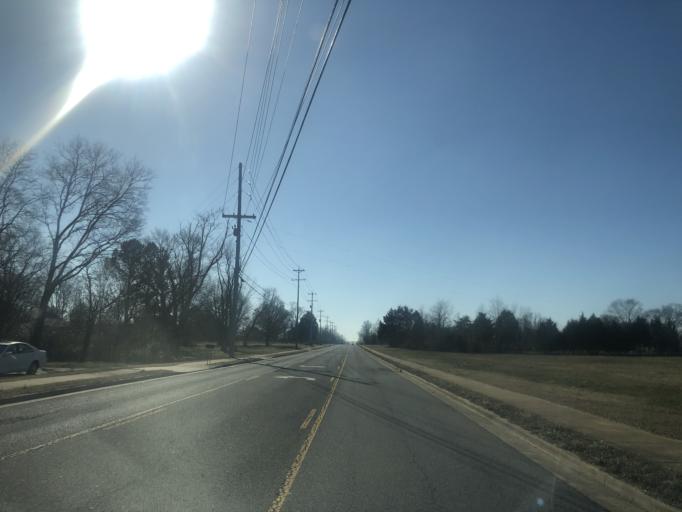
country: US
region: Tennessee
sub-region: Rutherford County
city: Smyrna
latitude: 35.9082
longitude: -86.4731
